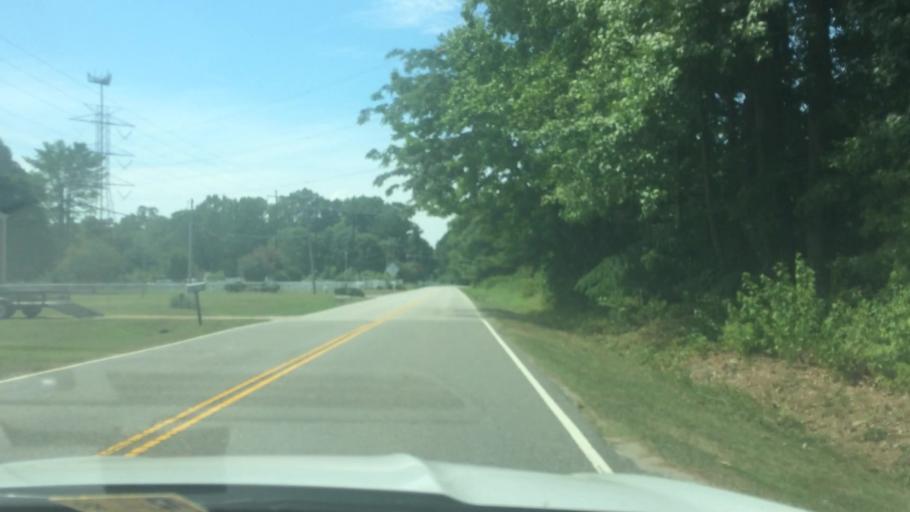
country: US
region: Virginia
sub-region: City of Poquoson
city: Poquoson
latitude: 37.1205
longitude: -76.4323
